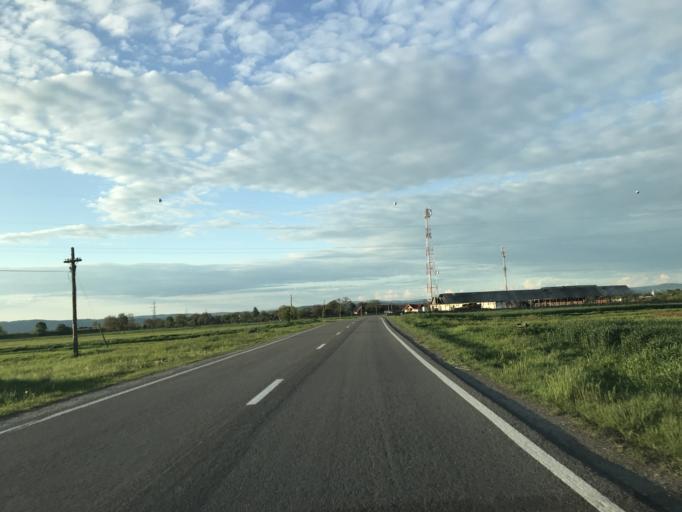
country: RO
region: Sibiu
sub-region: Comuna Cartisoara
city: Cartisoara
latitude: 45.7183
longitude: 24.5702
